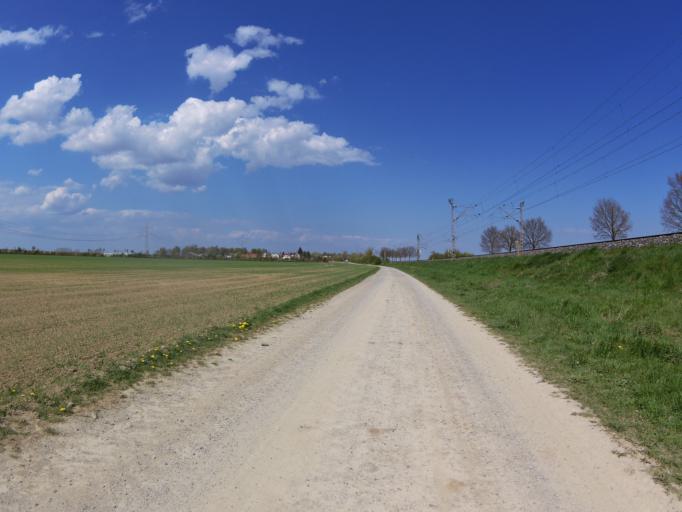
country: DE
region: Bavaria
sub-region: Regierungsbezirk Unterfranken
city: Oberpleichfeld
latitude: 49.8459
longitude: 10.1026
